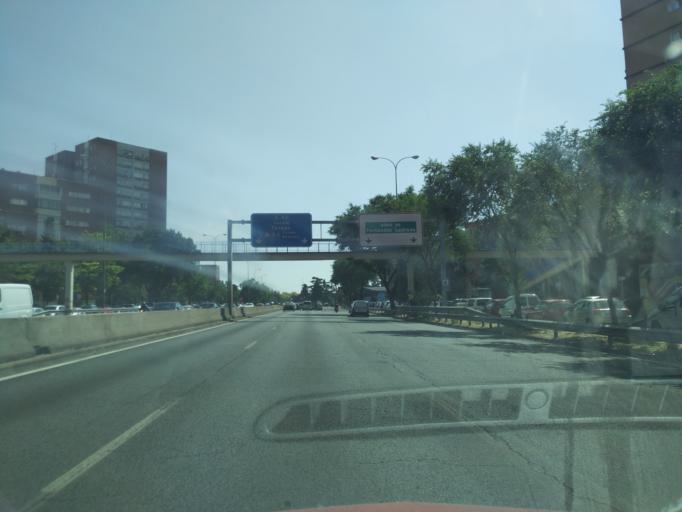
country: ES
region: Madrid
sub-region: Provincia de Madrid
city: Carabanchel
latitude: 40.3883
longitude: -3.7145
